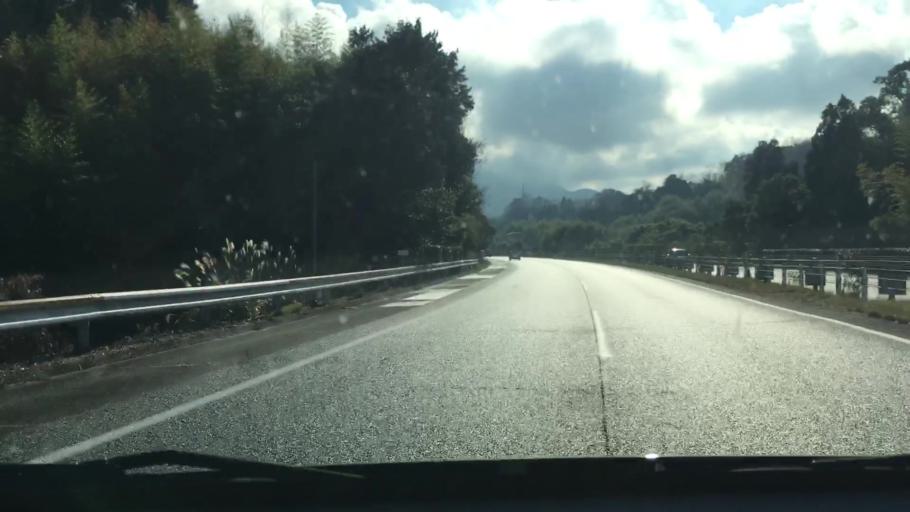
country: JP
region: Kumamoto
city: Matsubase
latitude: 32.5593
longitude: 130.6965
